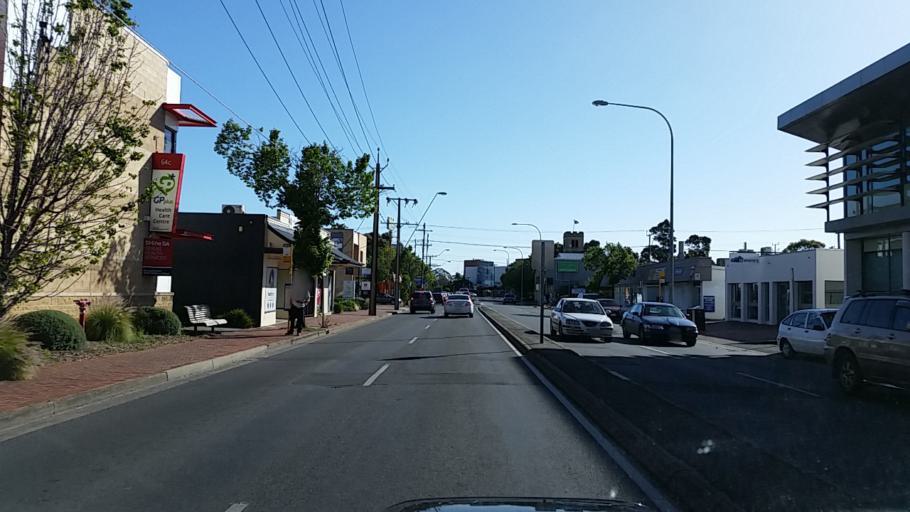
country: AU
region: South Australia
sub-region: Charles Sturt
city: Woodville West
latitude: -34.8791
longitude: 138.5367
